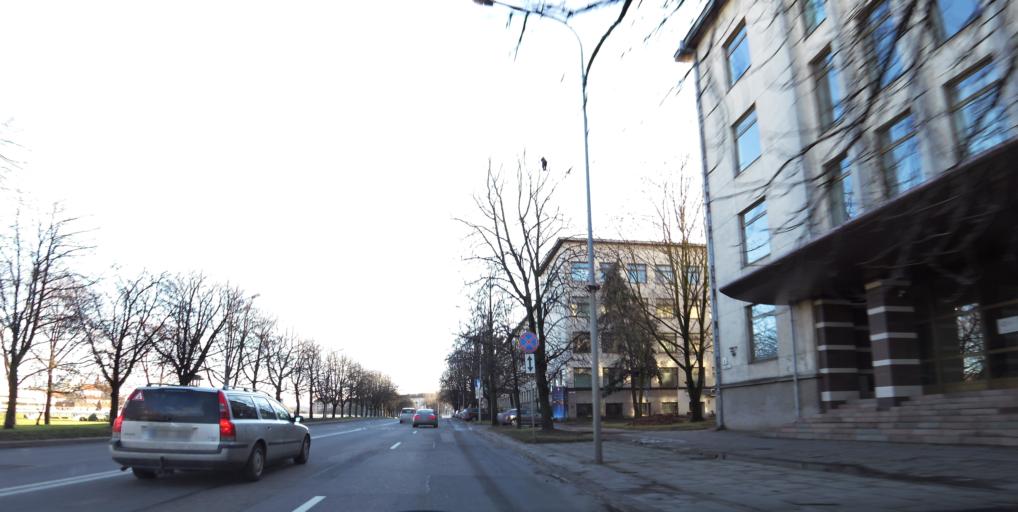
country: LT
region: Vilnius County
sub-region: Vilnius
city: Vilnius
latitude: 54.6943
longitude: 25.2684
